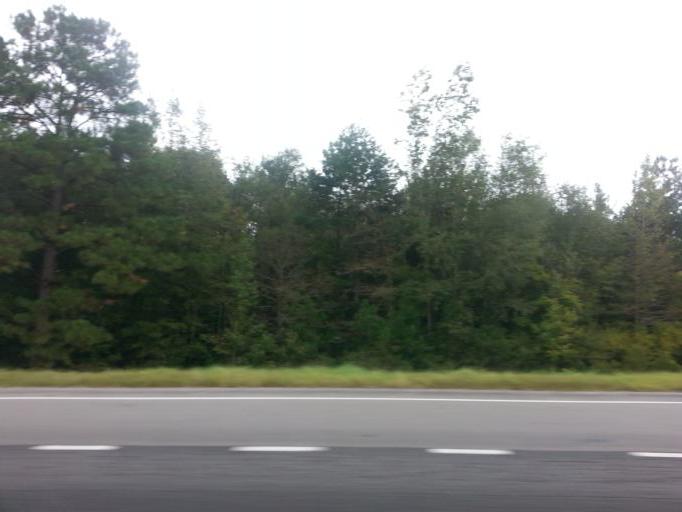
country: US
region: Alabama
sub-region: Butler County
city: Georgiana
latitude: 31.5740
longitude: -86.8493
